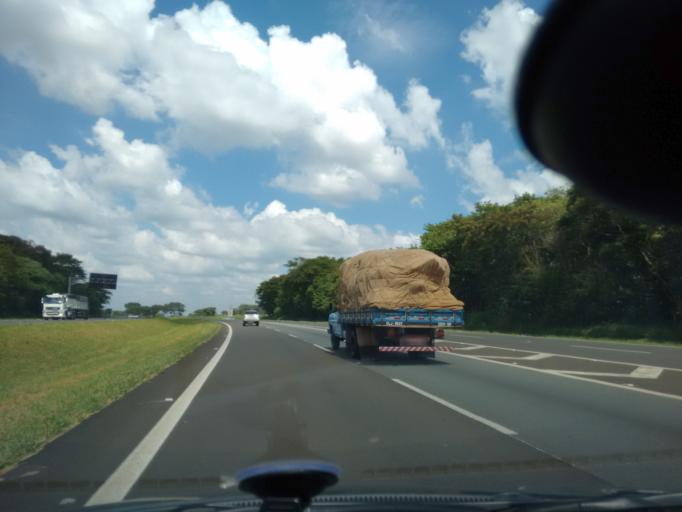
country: BR
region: Sao Paulo
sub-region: Santa Barbara D'Oeste
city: Santa Barbara d'Oeste
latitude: -22.7724
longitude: -47.4456
